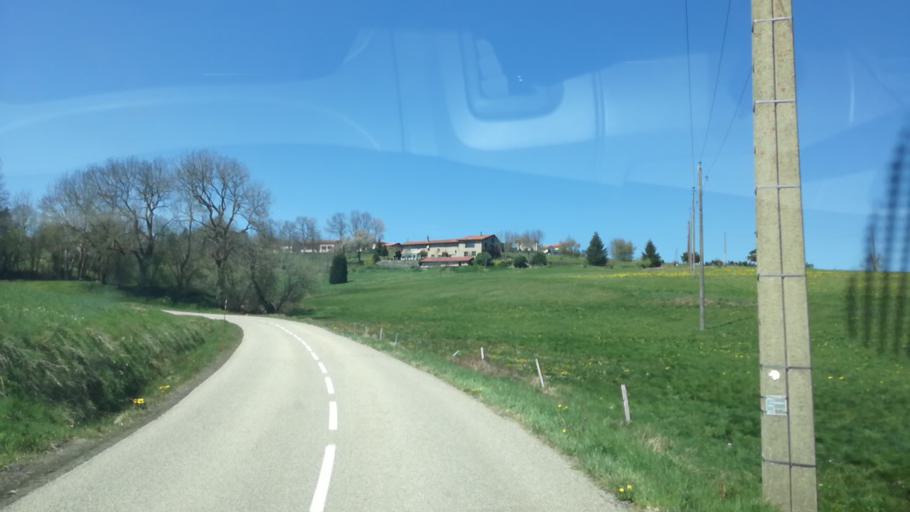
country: FR
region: Rhone-Alpes
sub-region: Departement de la Loire
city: Jonzieux
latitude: 45.3107
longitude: 4.3689
